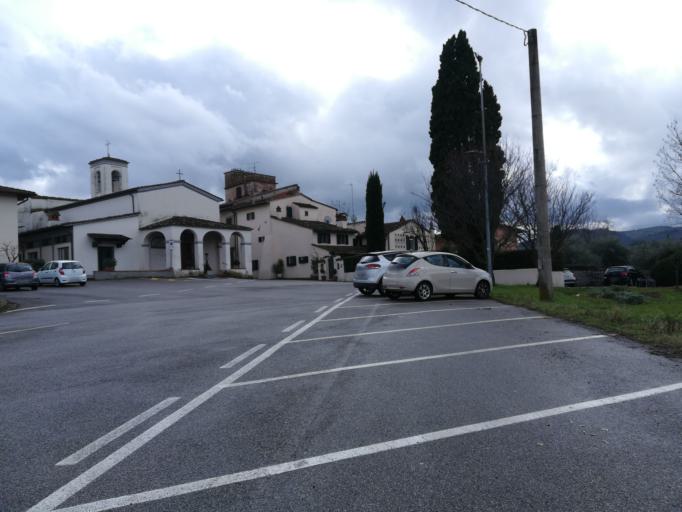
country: IT
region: Tuscany
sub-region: Provincia di Prato
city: Poggio A Caiano
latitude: 43.8068
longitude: 11.0490
